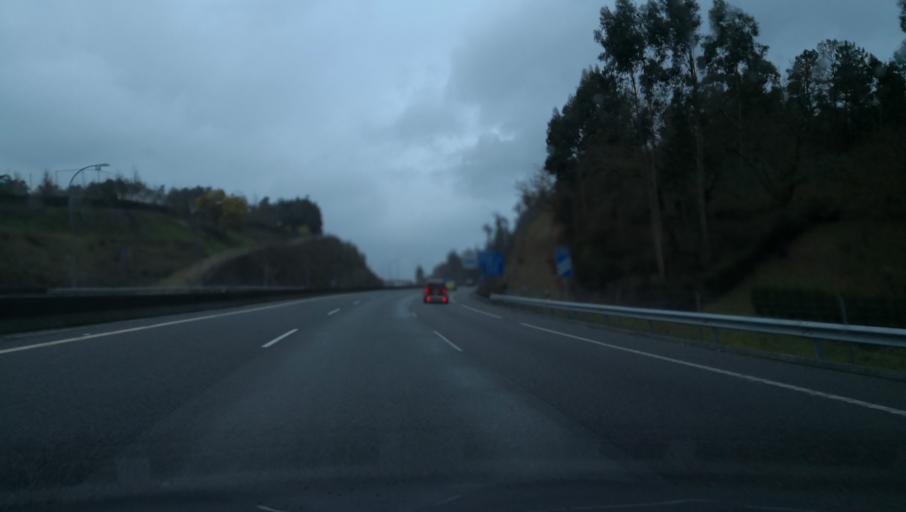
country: ES
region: Galicia
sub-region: Provincia da Coruna
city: Santiago de Compostela
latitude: 42.8489
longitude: -8.5328
